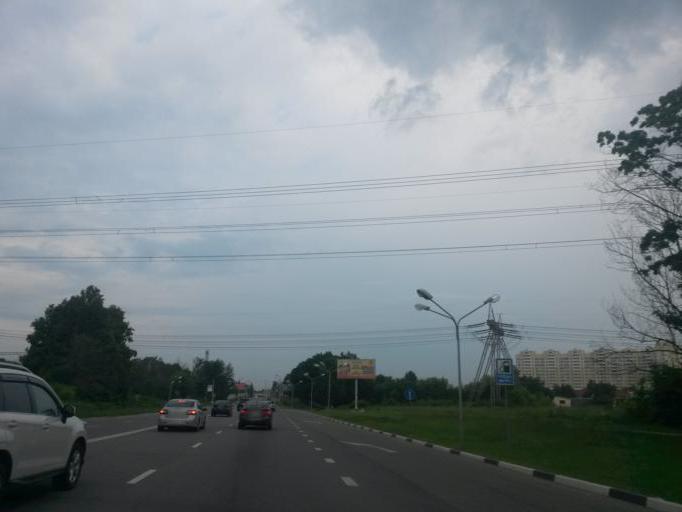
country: RU
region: Moskovskaya
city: Domodedovo
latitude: 55.4588
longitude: 37.7586
